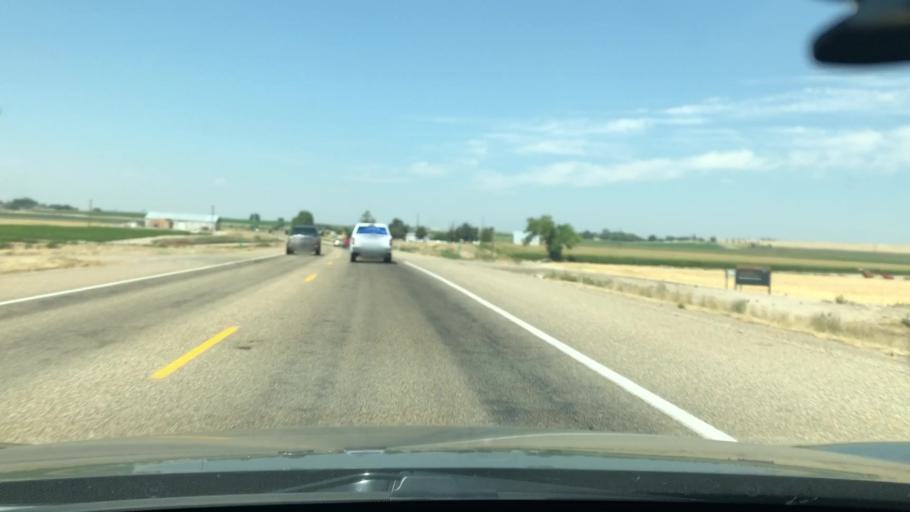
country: US
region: Idaho
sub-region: Canyon County
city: Parma
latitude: 43.8029
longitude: -116.9523
